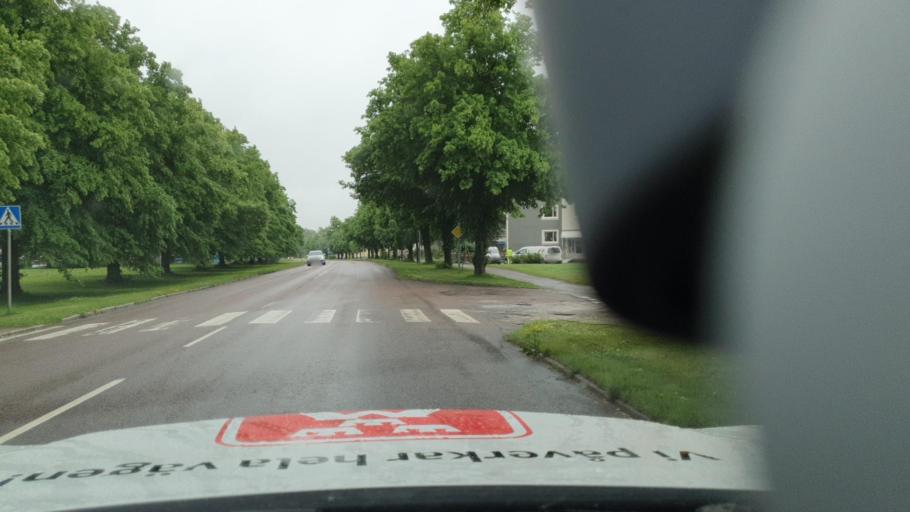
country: SE
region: Vaermland
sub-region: Kristinehamns Kommun
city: Kristinehamn
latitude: 59.3022
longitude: 14.1130
